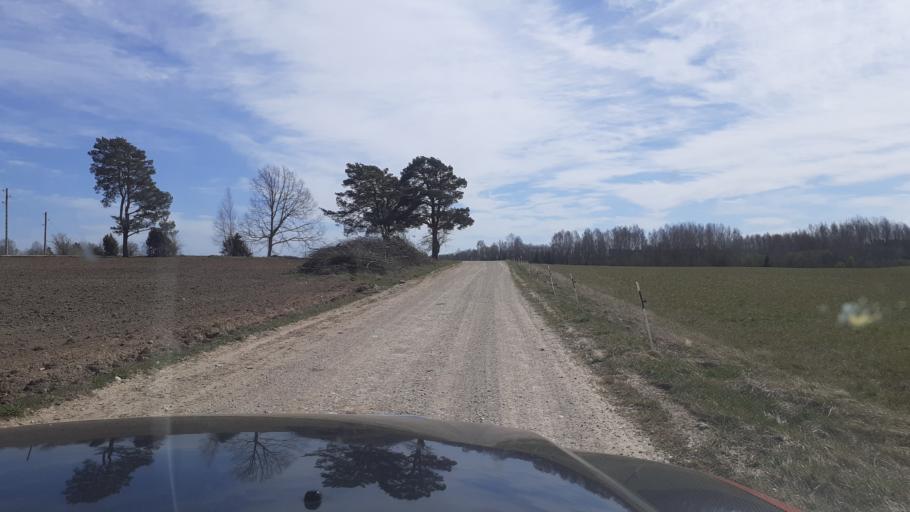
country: LV
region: Kuldigas Rajons
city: Kuldiga
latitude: 56.8389
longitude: 21.9910
